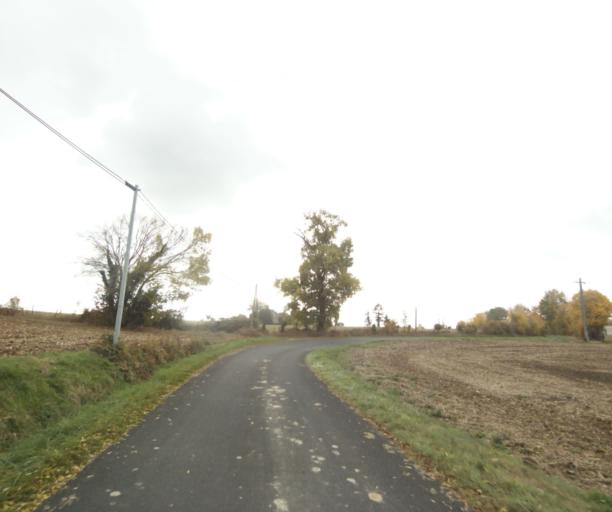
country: FR
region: Poitou-Charentes
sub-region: Departement de la Charente-Maritime
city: Saint-Georges-des-Coteaux
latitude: 45.7797
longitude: -0.6796
